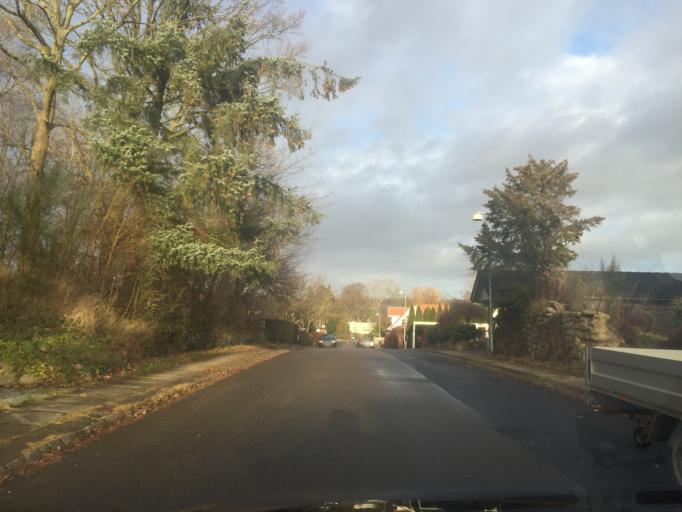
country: DK
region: Capital Region
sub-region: Fureso Kommune
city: Vaerlose
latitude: 55.7564
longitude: 12.4053
